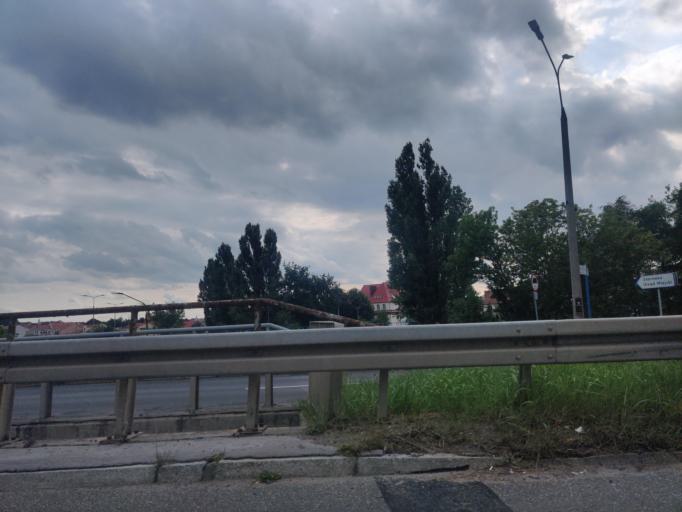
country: PL
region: Greater Poland Voivodeship
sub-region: Konin
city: Konin
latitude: 52.2132
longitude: 18.2587
